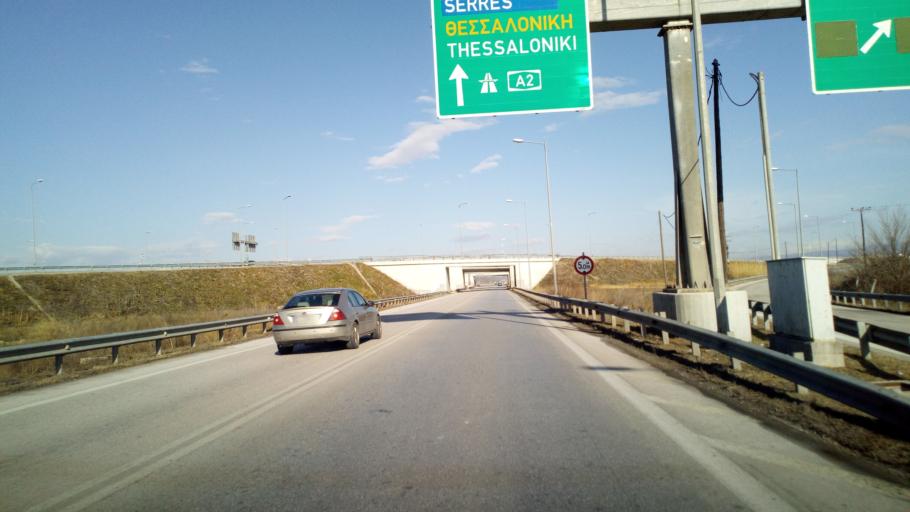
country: GR
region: Central Macedonia
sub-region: Nomos Thessalonikis
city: Lagyna
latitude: 40.7357
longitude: 23.0120
